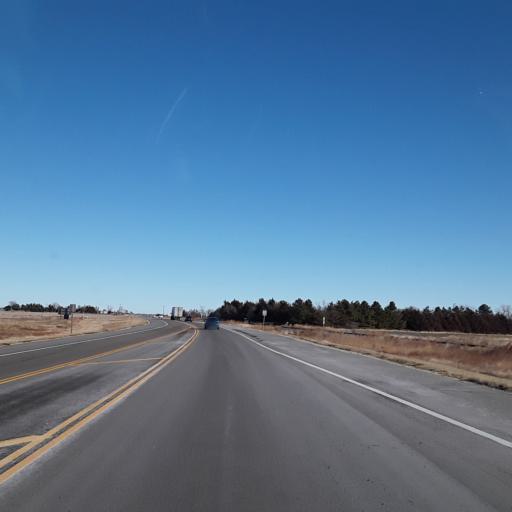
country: US
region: Kansas
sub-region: Pawnee County
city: Larned
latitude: 38.1901
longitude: -99.0825
